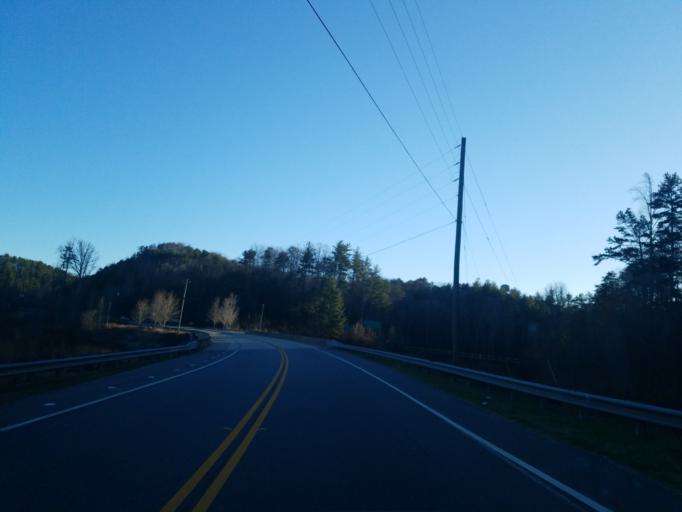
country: US
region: Georgia
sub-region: Lumpkin County
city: Dahlonega
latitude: 34.5481
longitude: -83.9727
